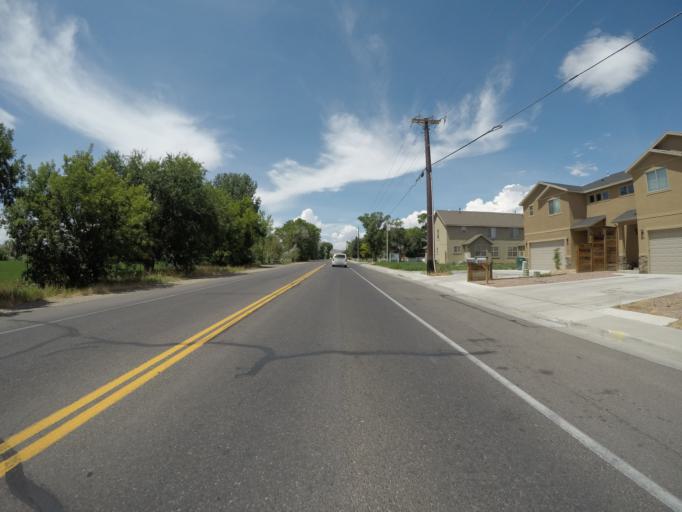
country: US
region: Utah
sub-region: Uintah County
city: Vernal
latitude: 40.4484
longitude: -109.5409
